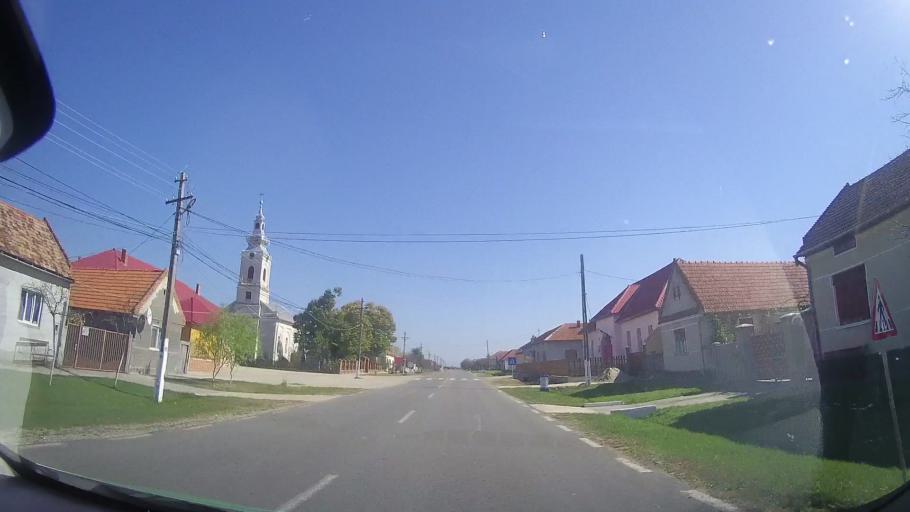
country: RO
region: Timis
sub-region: Comuna Bethausen
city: Bethausen
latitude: 45.7937
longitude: 21.9656
